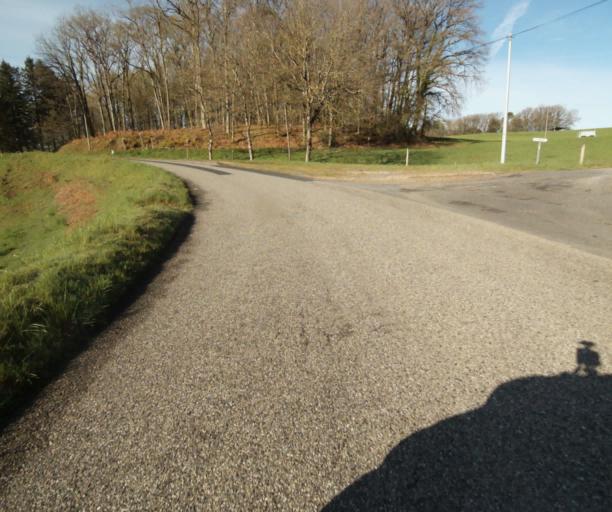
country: FR
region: Limousin
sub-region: Departement de la Correze
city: Laguenne
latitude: 45.2781
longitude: 1.8558
